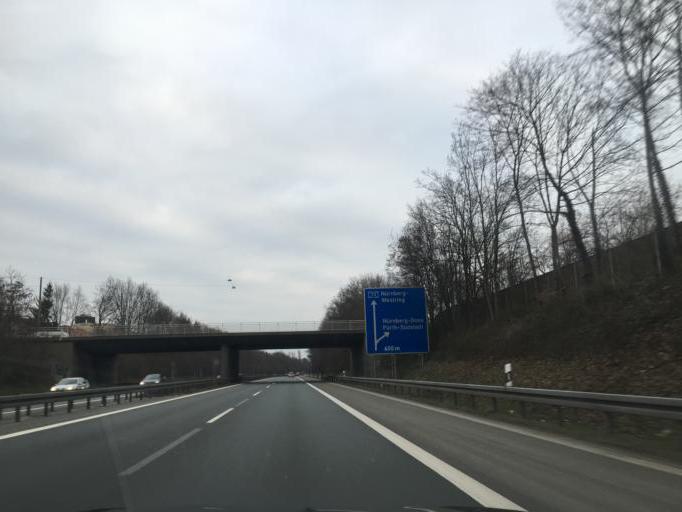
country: DE
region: Bavaria
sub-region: Regierungsbezirk Mittelfranken
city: Furth
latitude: 49.4766
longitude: 11.0103
